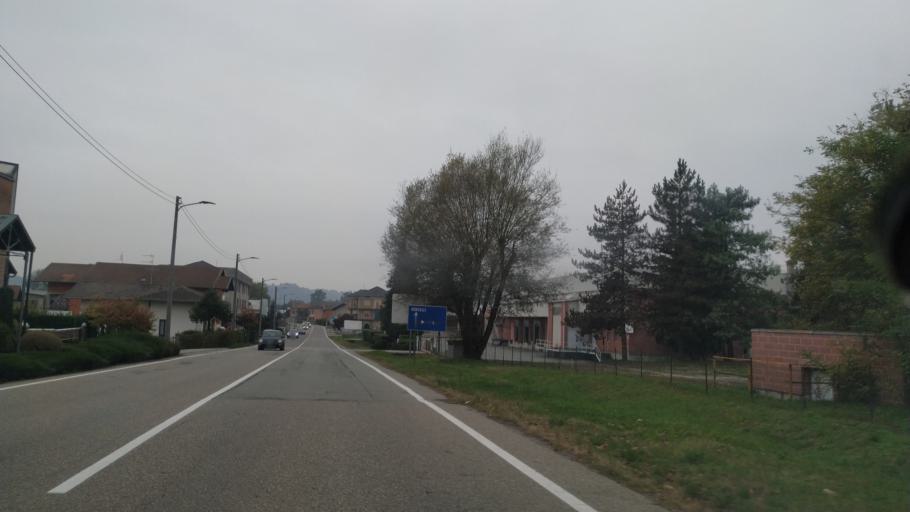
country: IT
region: Piedmont
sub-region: Provincia di Biella
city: Cerreto Castello
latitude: 45.5617
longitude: 8.1736
